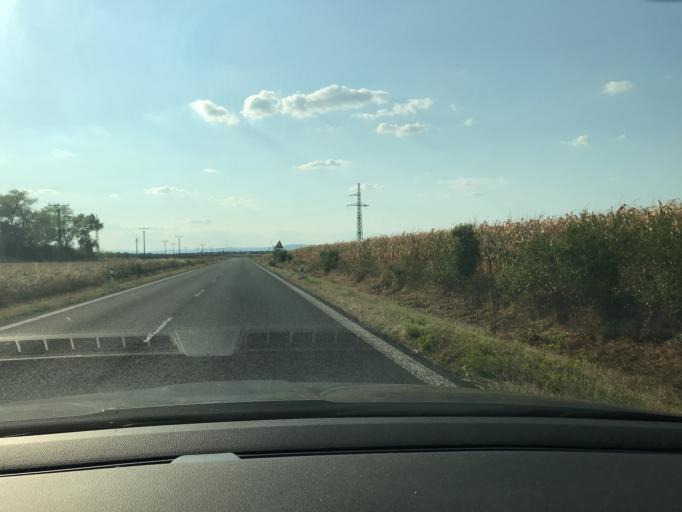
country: CZ
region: Ustecky
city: Zatec
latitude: 50.3826
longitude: 13.5721
